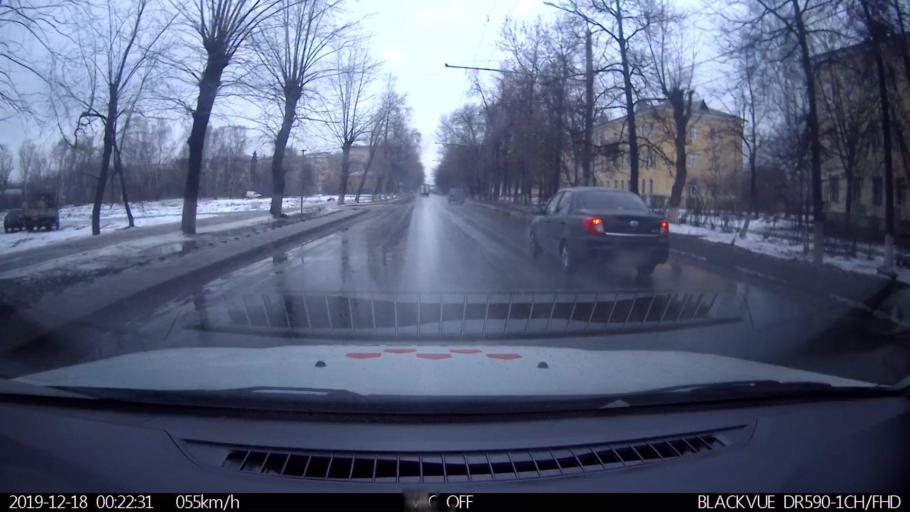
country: RU
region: Nizjnij Novgorod
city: Nizhniy Novgorod
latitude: 56.3325
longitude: 43.8849
